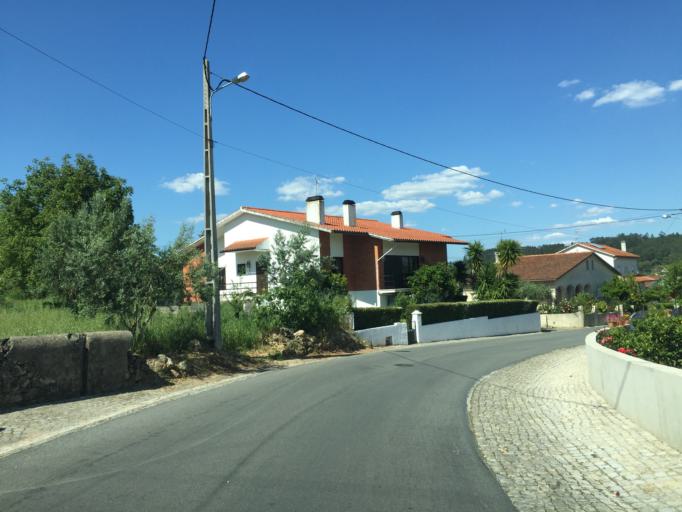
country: PT
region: Leiria
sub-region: Alvaiazere
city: Alvaiazere
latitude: 39.8219
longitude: -8.3958
